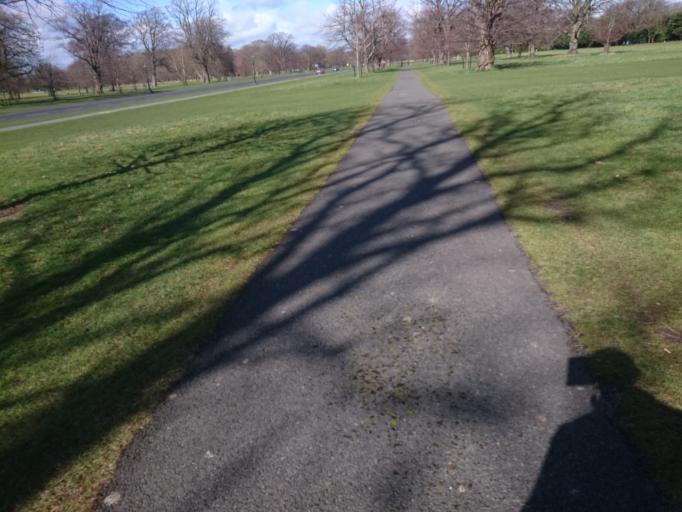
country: IE
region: Leinster
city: Cabra
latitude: 53.3574
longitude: -6.3185
